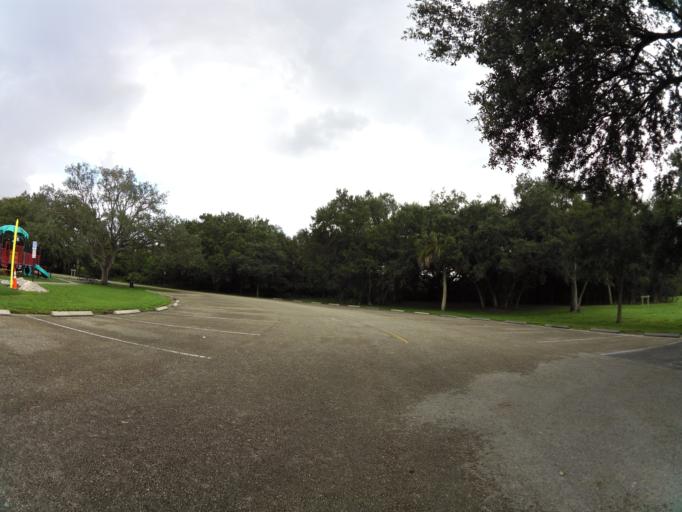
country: US
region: Florida
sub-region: Broward County
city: Cooper City
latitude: 26.0670
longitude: -80.2756
